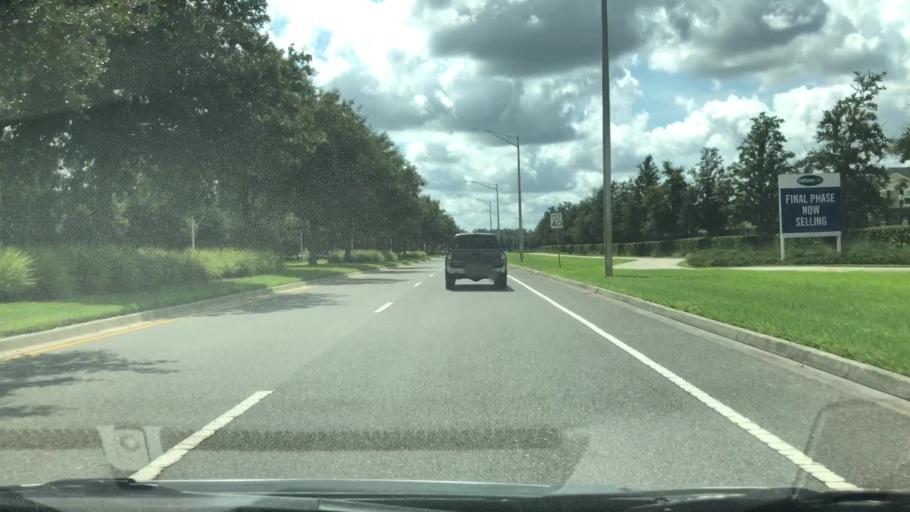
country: US
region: Florida
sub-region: Saint Johns County
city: Fruit Cove
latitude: 30.1152
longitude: -81.5201
